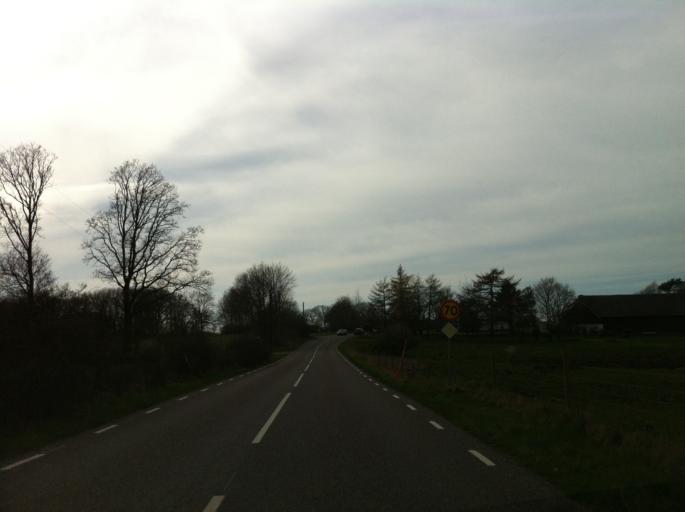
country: SE
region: Skane
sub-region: Hoganas Kommun
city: Hoganas
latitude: 56.2610
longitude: 12.5996
